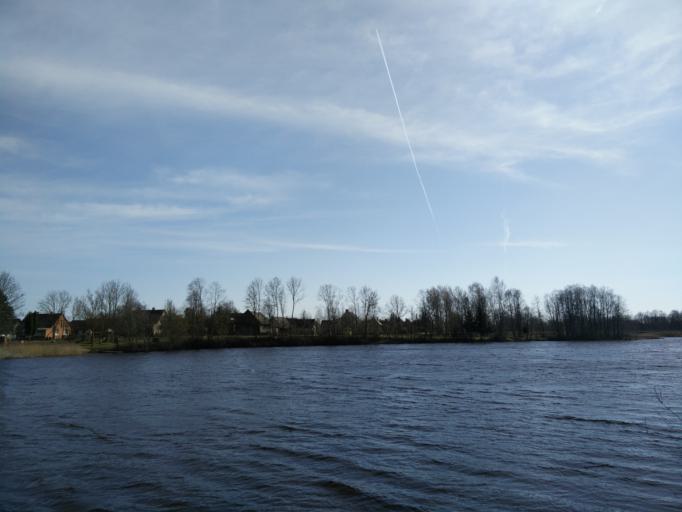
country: LT
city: Ariogala
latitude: 55.3929
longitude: 23.3309
